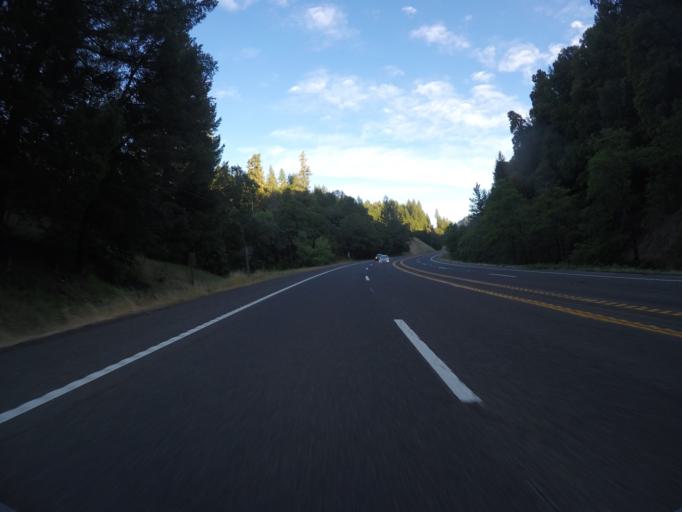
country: US
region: California
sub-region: Mendocino County
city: Laytonville
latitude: 39.5709
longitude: -123.4363
